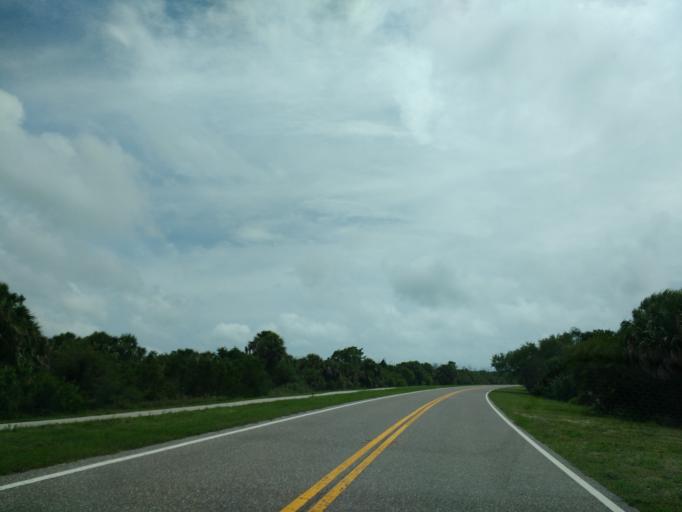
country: US
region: Florida
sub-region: Pinellas County
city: Tierra Verde
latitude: 27.6305
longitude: -82.7028
